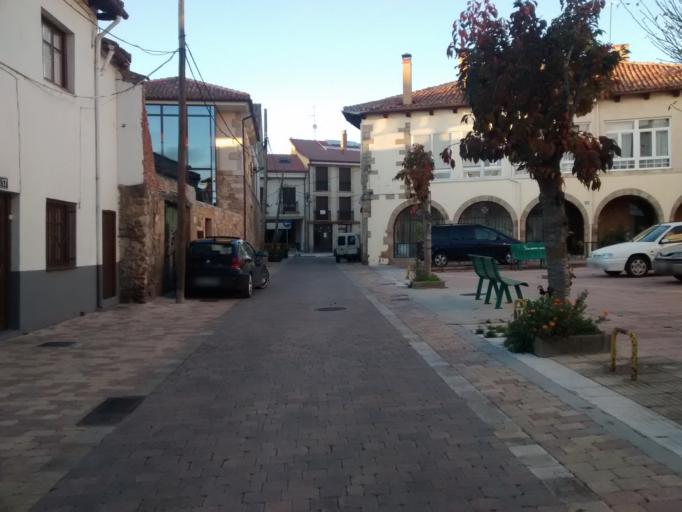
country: ES
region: Castille and Leon
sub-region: Provincia de Palencia
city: Aguilar de Campoo
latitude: 42.7927
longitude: -4.2576
